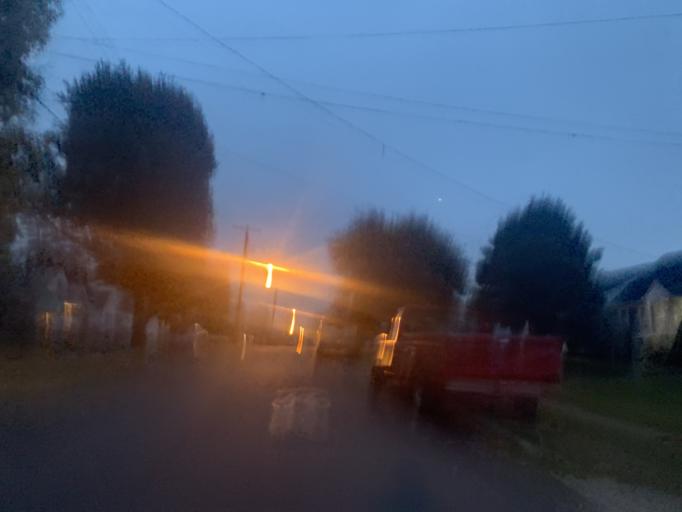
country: US
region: Kentucky
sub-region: Jefferson County
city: Louisville
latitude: 38.2150
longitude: -85.7704
